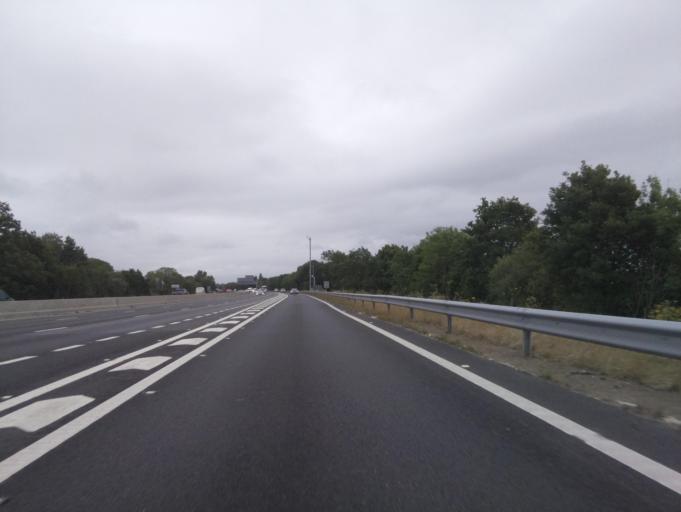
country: GB
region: England
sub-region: West Sussex
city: Copthorne
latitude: 51.1633
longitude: -0.1314
